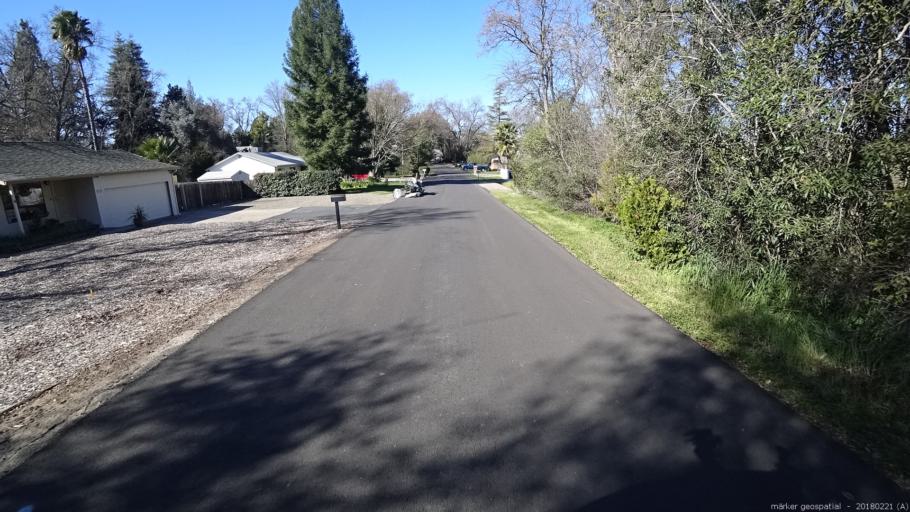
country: US
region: California
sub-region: Sacramento County
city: Orangevale
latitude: 38.6823
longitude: -121.2407
